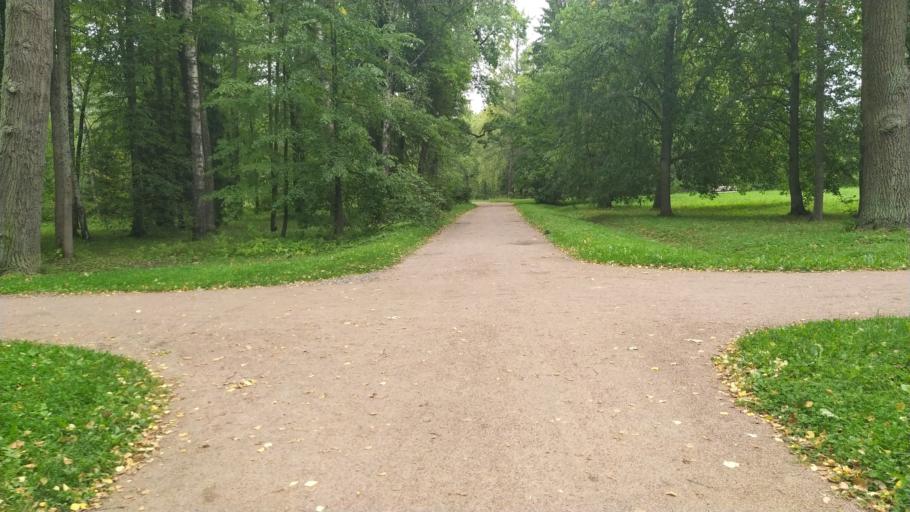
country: RU
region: St.-Petersburg
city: Pushkin
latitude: 59.7200
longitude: 30.3829
